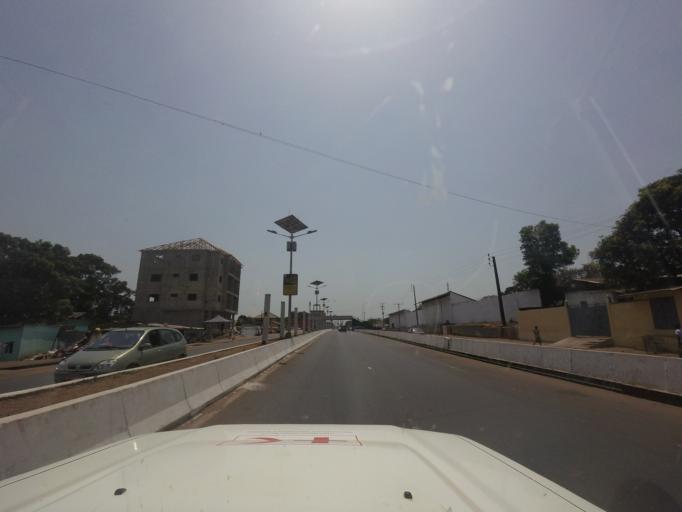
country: GN
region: Conakry
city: Conakry
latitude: 9.5571
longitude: -13.6489
